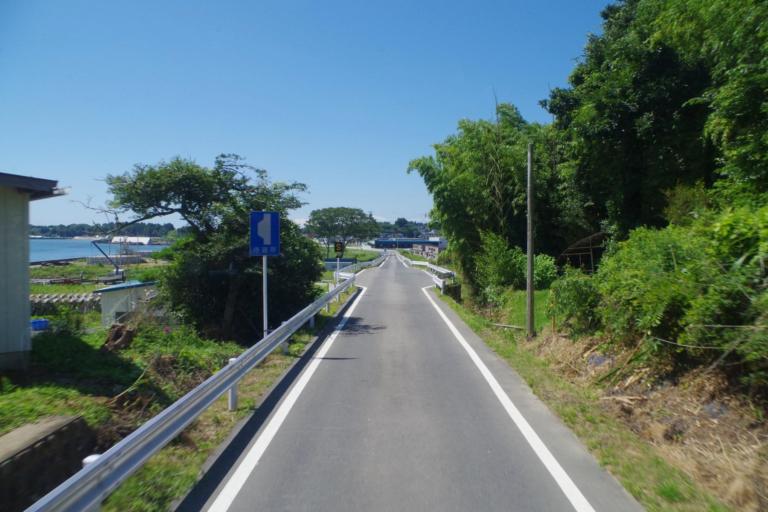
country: JP
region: Iwate
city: Ofunato
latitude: 38.8583
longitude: 141.5828
